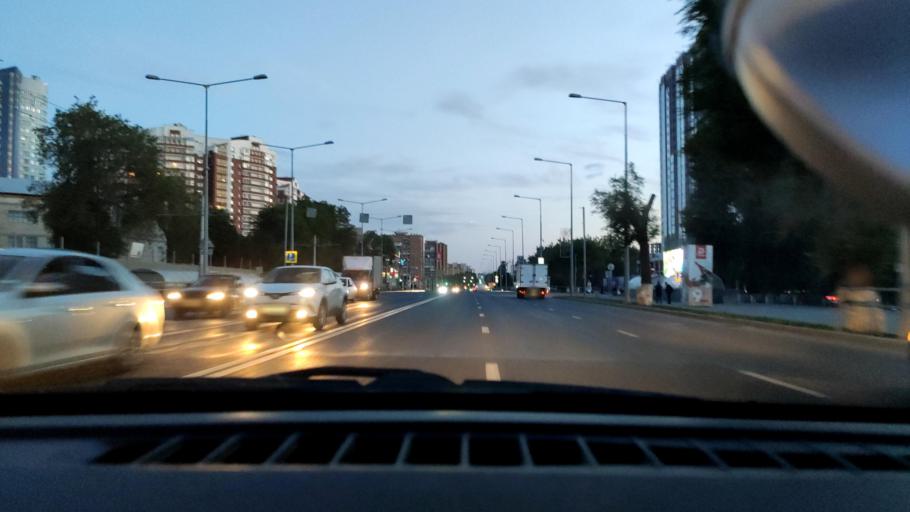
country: RU
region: Samara
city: Samara
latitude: 53.2190
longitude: 50.1477
